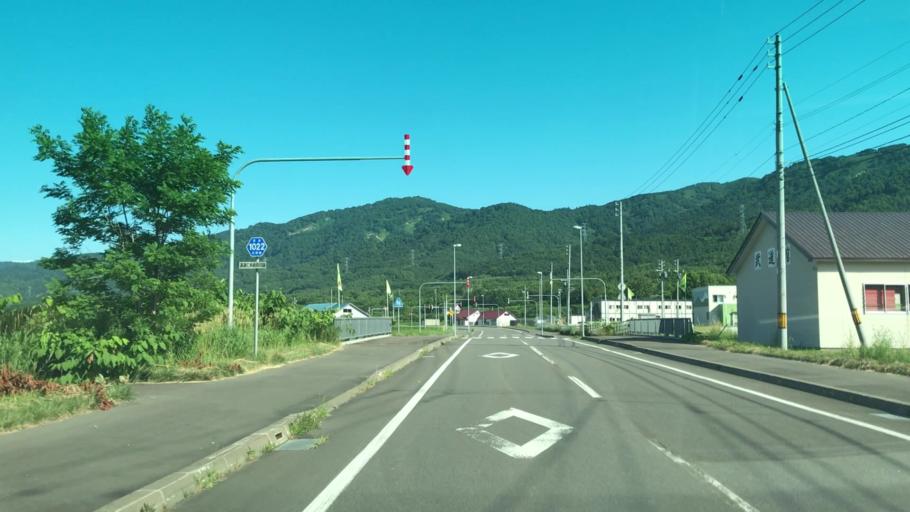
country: JP
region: Hokkaido
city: Yoichi
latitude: 43.0407
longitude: 140.7336
